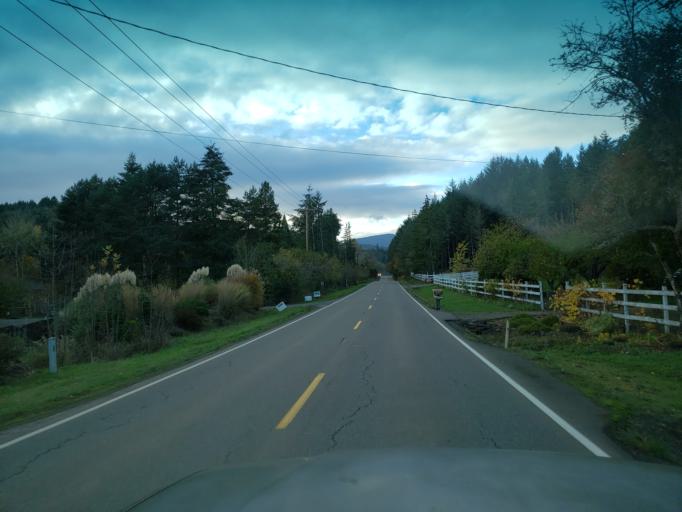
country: US
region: Oregon
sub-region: Yamhill County
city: McMinnville
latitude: 45.2257
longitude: -123.2645
